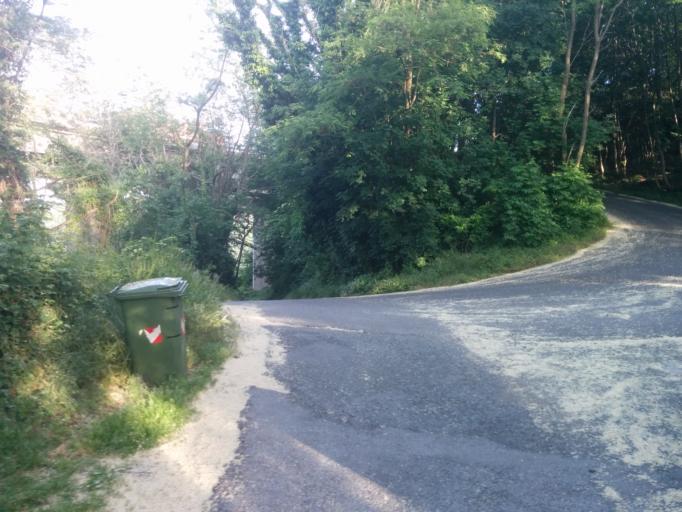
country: IT
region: Liguria
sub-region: Provincia di Genova
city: Mele
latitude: 44.4571
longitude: 8.7436
